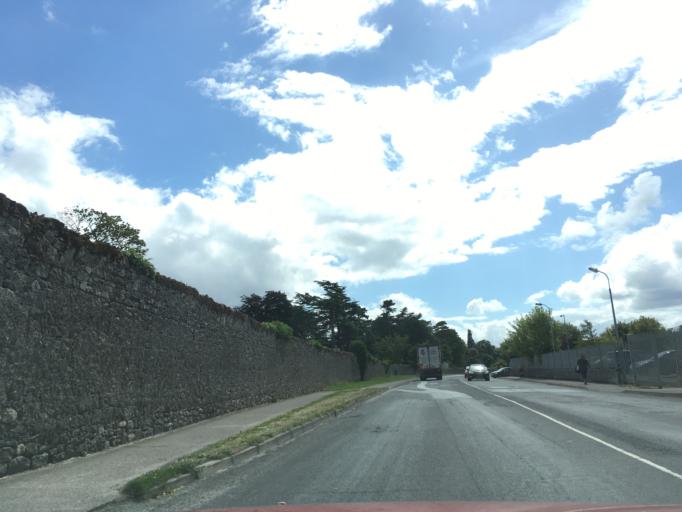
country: IE
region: Munster
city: Cahir
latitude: 52.3735
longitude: -7.9309
